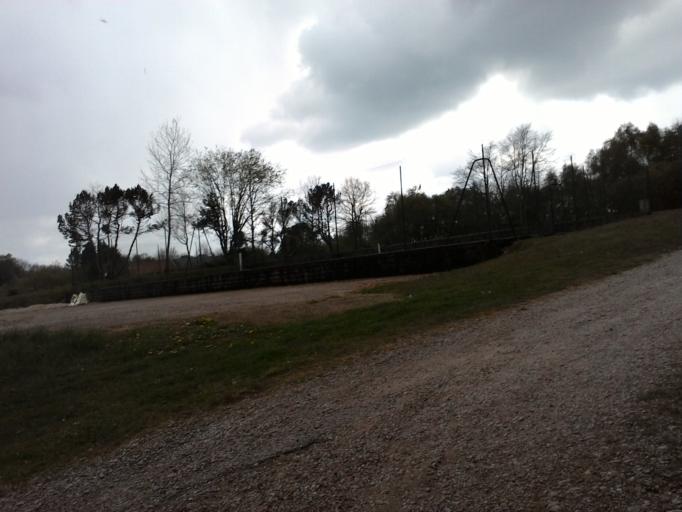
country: FR
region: Bourgogne
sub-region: Departement de la Cote-d'Or
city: Saulieu
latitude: 47.1878
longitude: 4.0716
